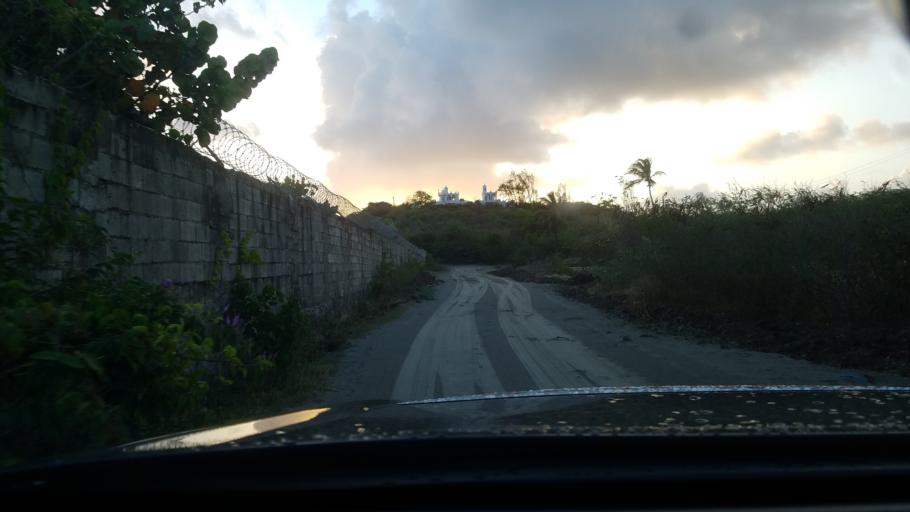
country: LC
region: Gros-Islet
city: Gros Islet
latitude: 14.0910
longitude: -60.9295
